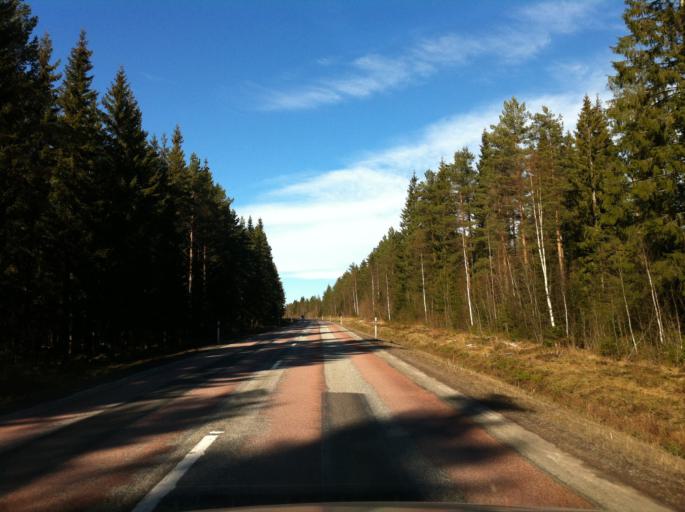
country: SE
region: Vaermland
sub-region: Filipstads Kommun
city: Filipstad
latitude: 59.7277
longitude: 14.2149
